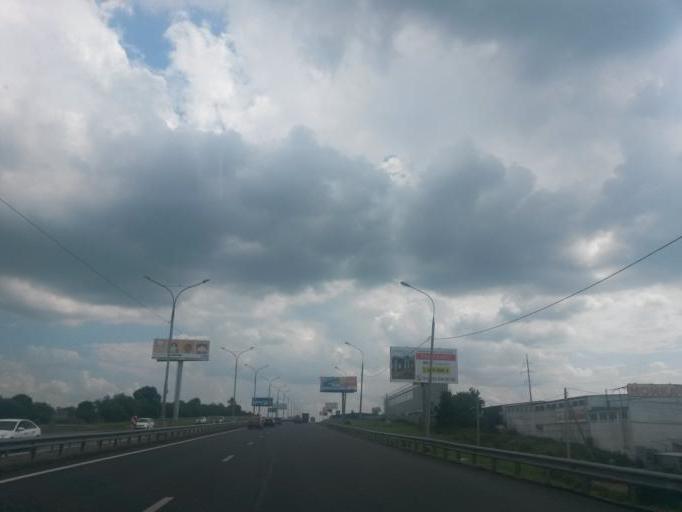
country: RU
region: Moskovskaya
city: Razvilka
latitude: 55.5750
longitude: 37.7606
